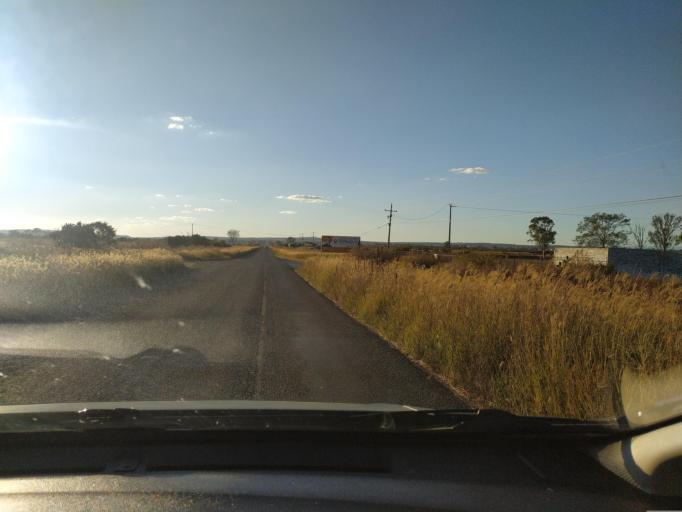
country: MX
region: Jalisco
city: San Julian
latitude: 21.0068
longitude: -102.1302
